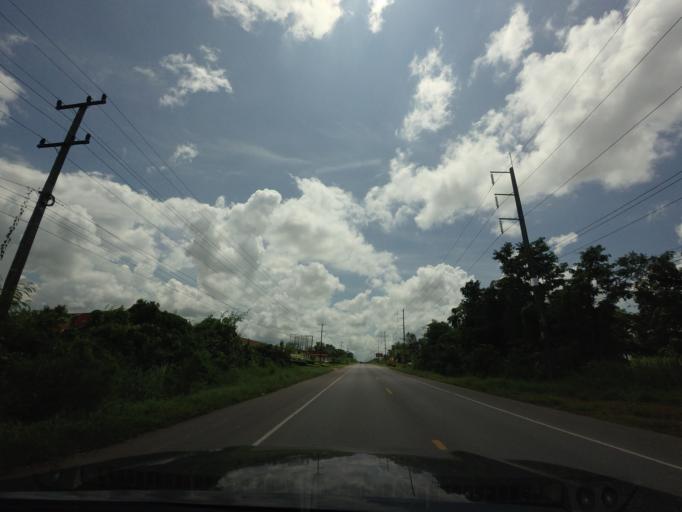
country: TH
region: Changwat Udon Thani
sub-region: Amphoe Ban Phue
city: Ban Phue
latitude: 17.6759
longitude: 102.5057
